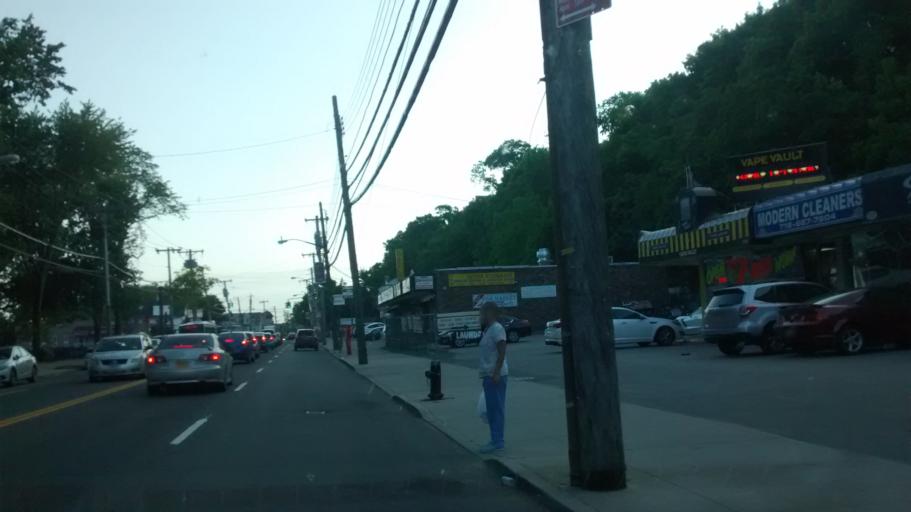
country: US
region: New York
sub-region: Richmond County
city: Staten Island
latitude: 40.5880
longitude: -74.1030
